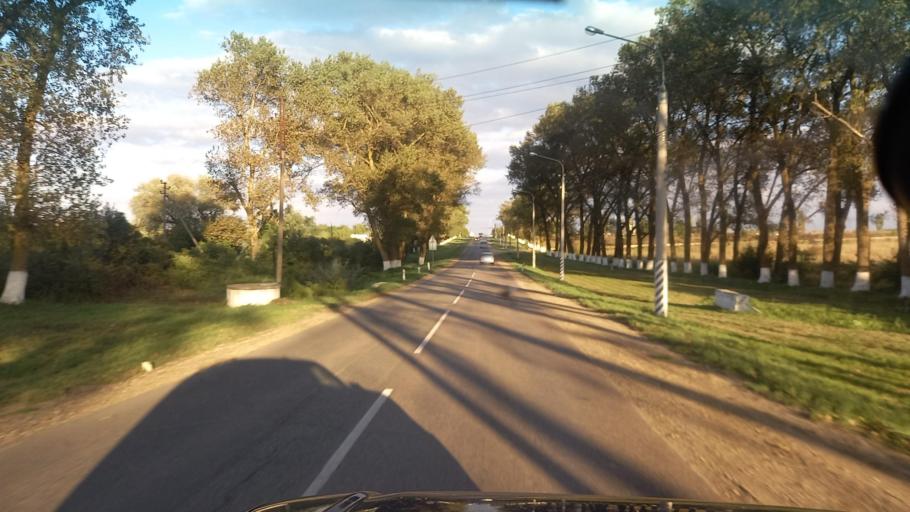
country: RU
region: Krasnodarskiy
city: Krymsk
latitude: 44.9393
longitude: 37.9385
